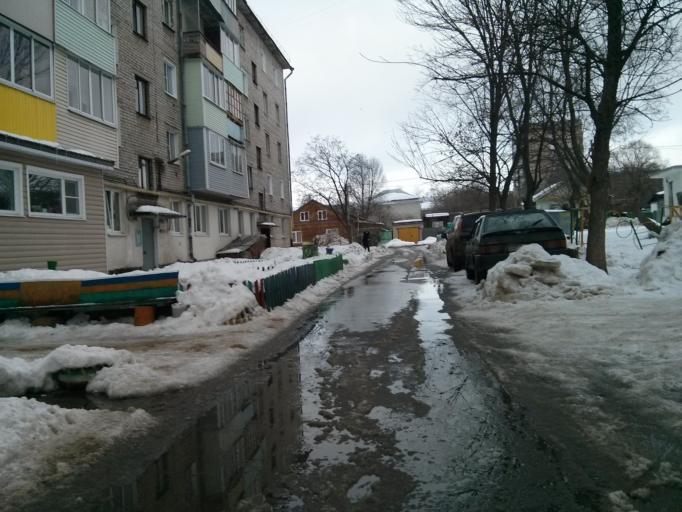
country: RU
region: Vladimir
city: Murom
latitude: 55.5660
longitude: 42.0550
